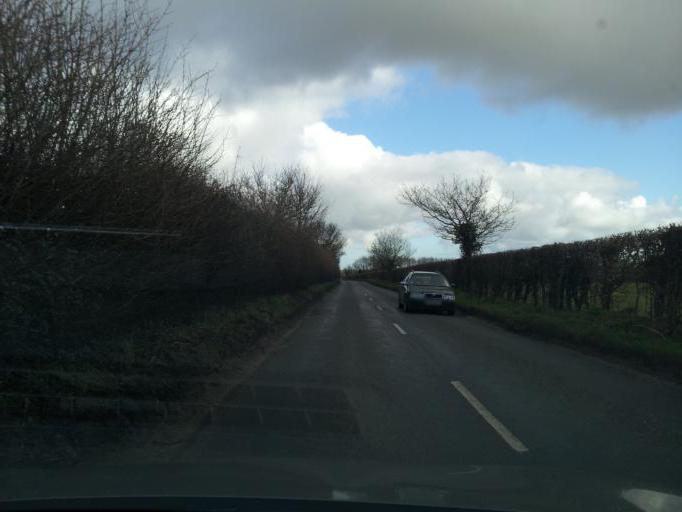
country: GB
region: England
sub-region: Norfolk
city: Mattishall
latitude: 52.6580
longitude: 1.1038
